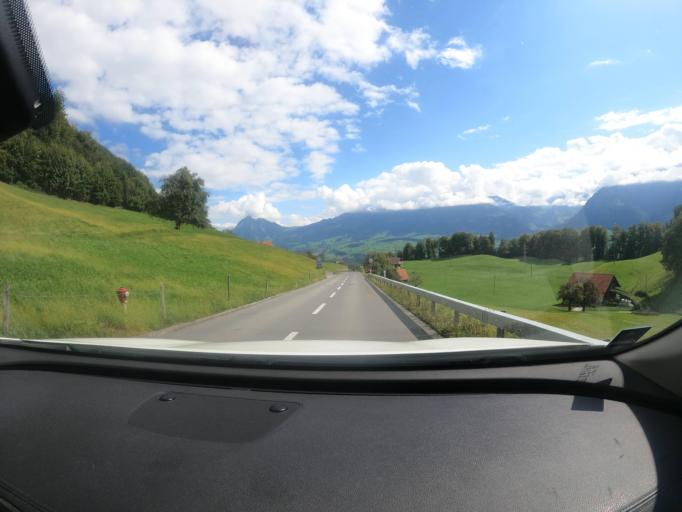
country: CH
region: Obwalden
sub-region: Obwalden
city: Sachseln
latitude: 46.8876
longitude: 8.2138
